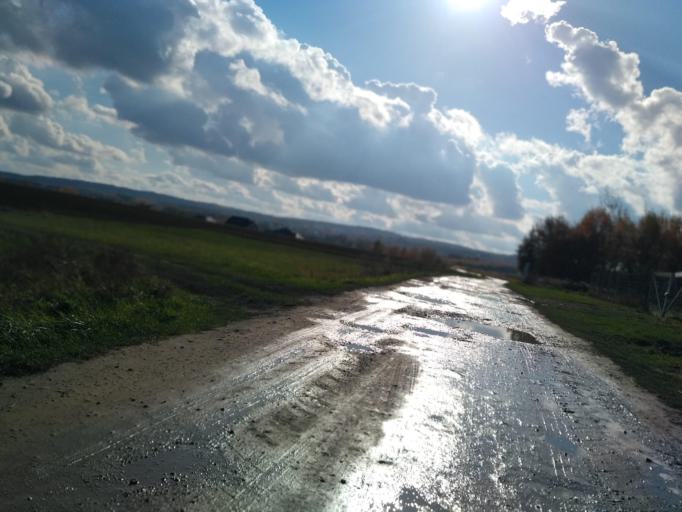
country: PL
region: Subcarpathian Voivodeship
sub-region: Powiat rzeszowski
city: Zglobien
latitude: 50.0024
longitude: 21.8618
